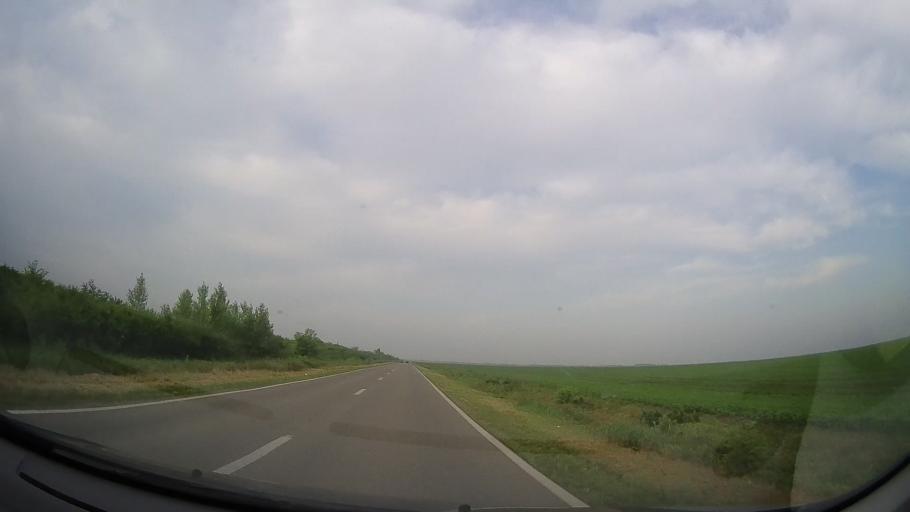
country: RO
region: Timis
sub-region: Comuna Peciu Nou
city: Peciu Nou
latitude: 45.6270
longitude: 21.0935
